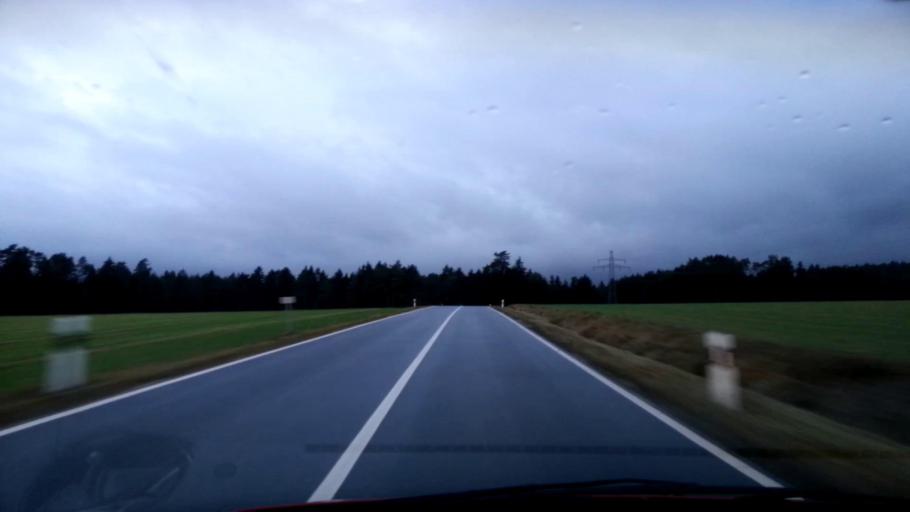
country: DE
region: Bavaria
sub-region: Upper Franconia
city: Konigsfeld
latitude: 49.9396
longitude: 11.2025
